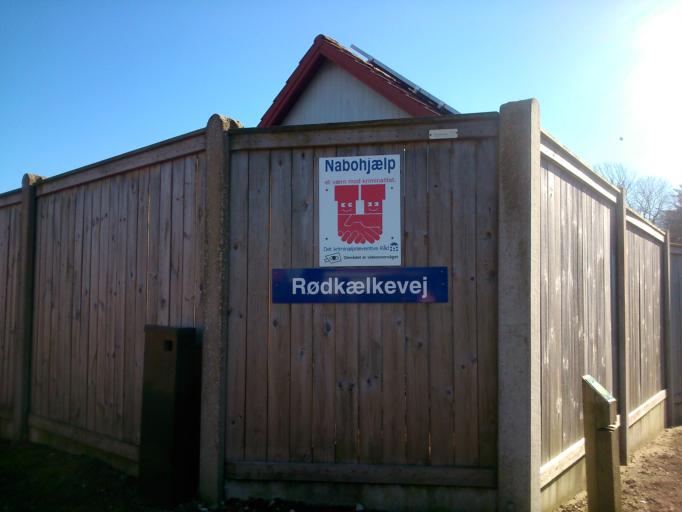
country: DK
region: Central Jutland
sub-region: Ringkobing-Skjern Kommune
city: Ringkobing
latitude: 56.0876
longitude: 8.2631
